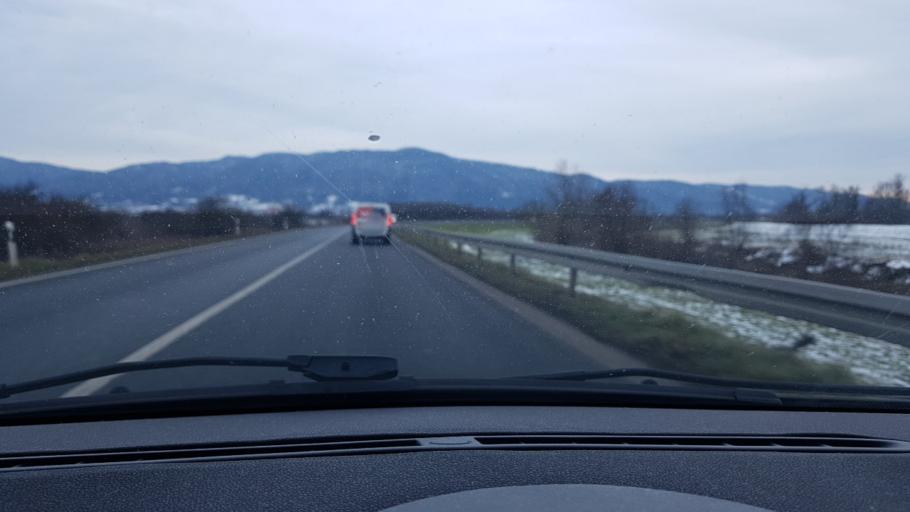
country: HR
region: Zagrebacka
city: Pojatno
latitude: 45.8935
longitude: 15.8187
